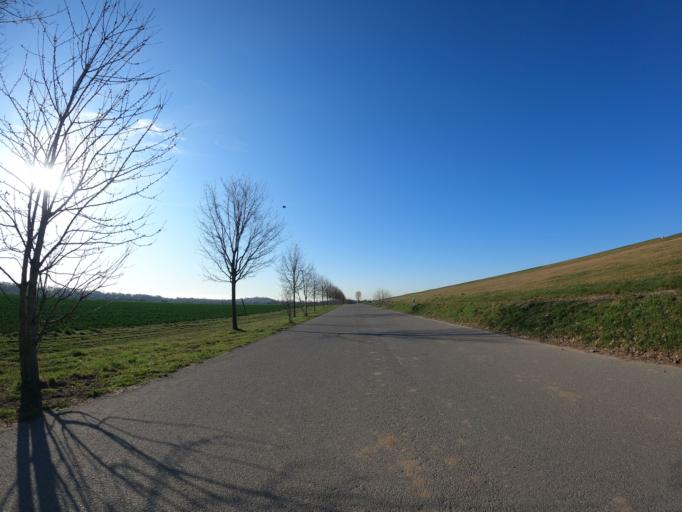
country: DE
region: Berlin
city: Gropiusstadt
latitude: 52.4140
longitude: 13.4627
